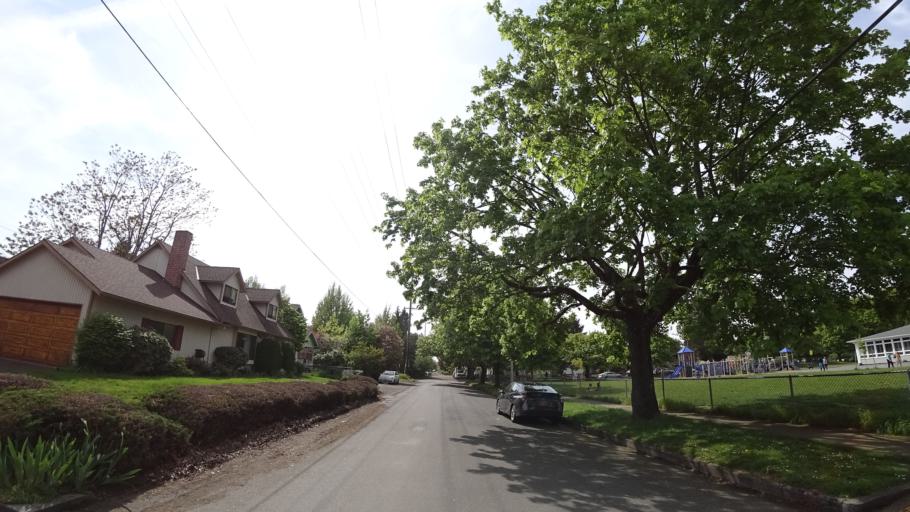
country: US
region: Oregon
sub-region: Clackamas County
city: Milwaukie
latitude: 45.4814
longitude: -122.6125
